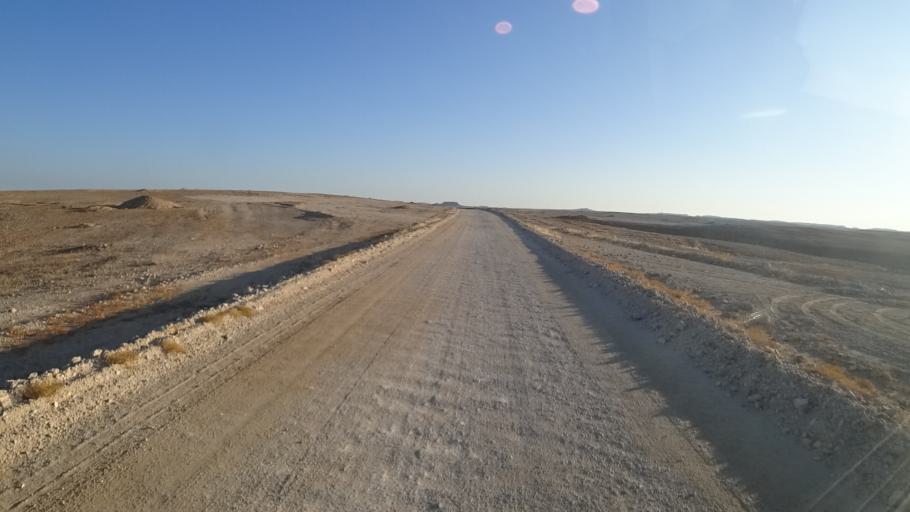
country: YE
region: Al Mahrah
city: Hawf
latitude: 17.1661
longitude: 53.3519
